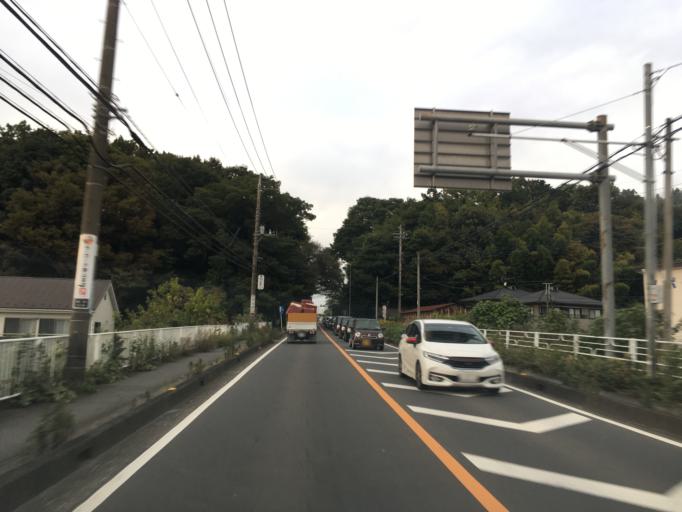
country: JP
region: Saitama
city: Sayama
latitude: 35.8578
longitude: 139.3805
